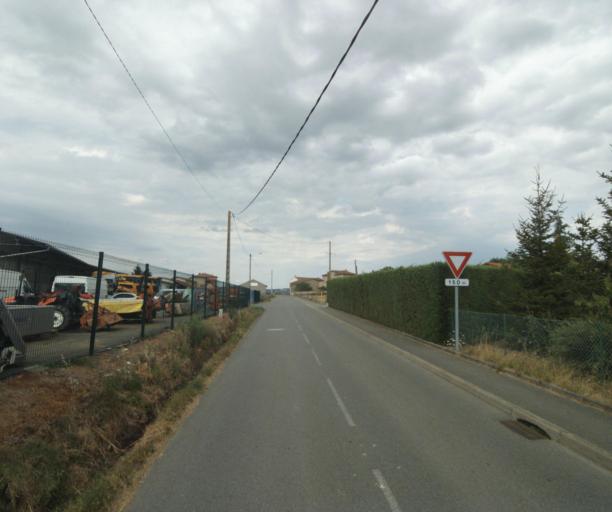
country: FR
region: Rhone-Alpes
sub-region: Departement du Rhone
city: Bully
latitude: 45.8769
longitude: 4.5560
